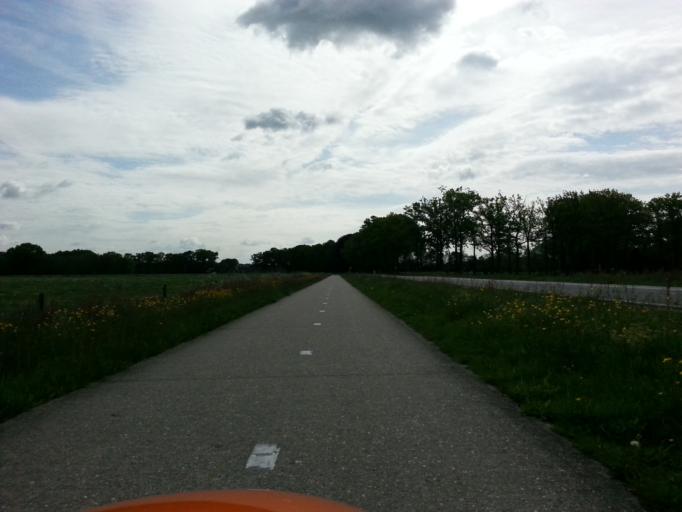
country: NL
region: Utrecht
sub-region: Gemeente Utrechtse Heuvelrug
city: Overberg
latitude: 52.0887
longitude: 5.5010
